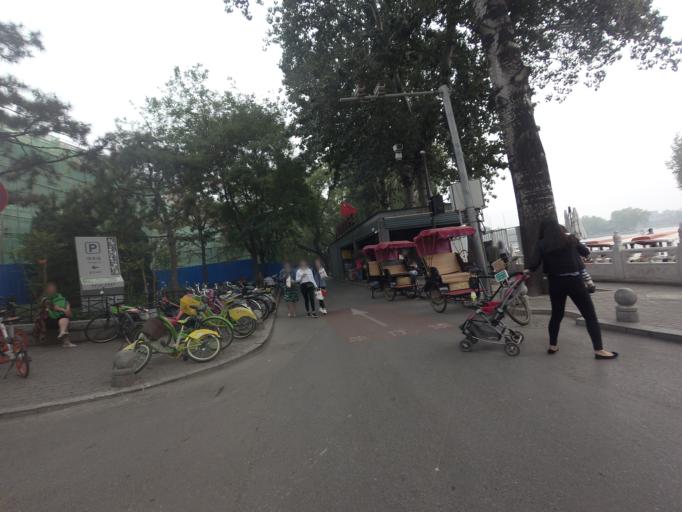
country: CN
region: Beijing
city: Jingshan
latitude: 39.9369
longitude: 116.3886
